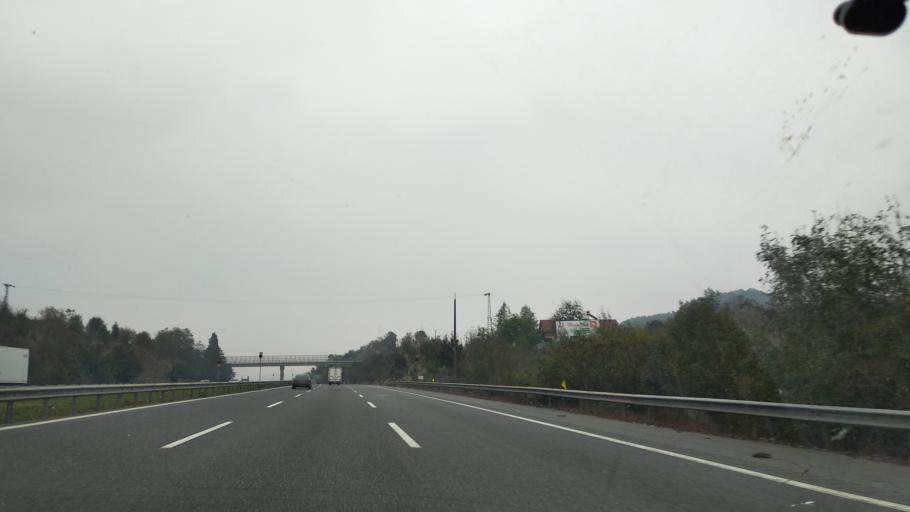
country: TR
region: Duzce
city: Gumusova
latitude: 40.8151
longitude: 30.9087
